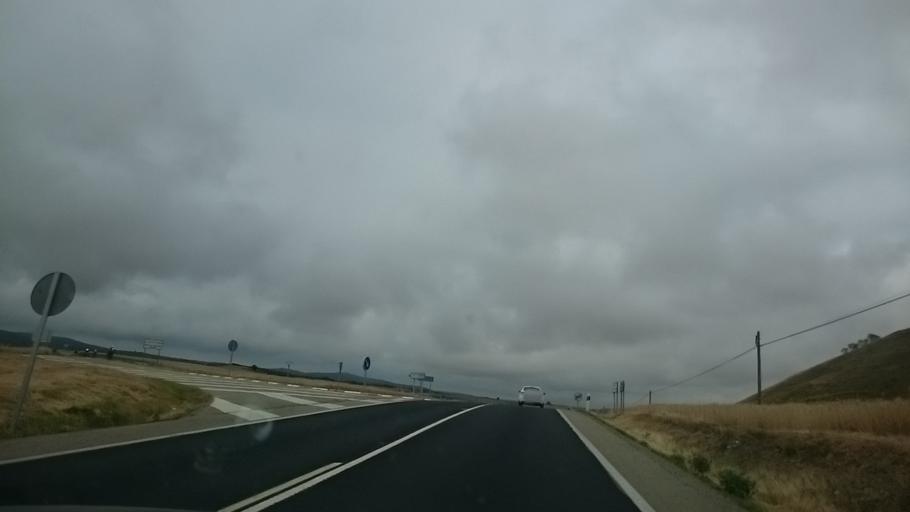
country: ES
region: Castille and Leon
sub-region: Provincia de Burgos
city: Castildelgado
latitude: 42.4342
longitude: -3.0935
